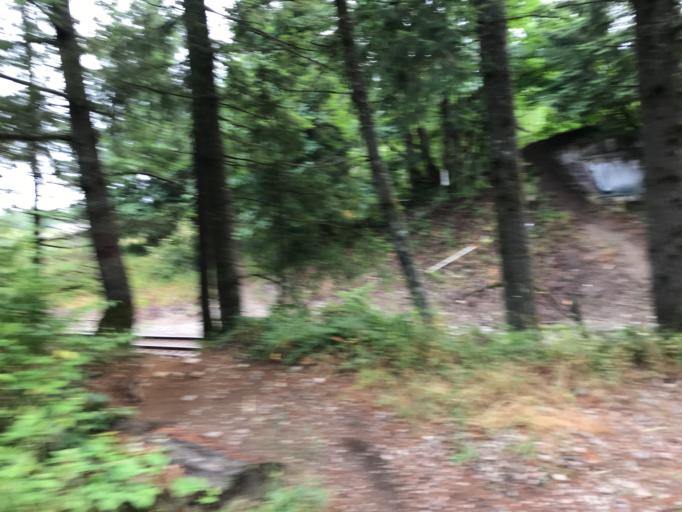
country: US
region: Washington
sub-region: King County
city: Ravensdale
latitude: 47.3470
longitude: -122.0196
